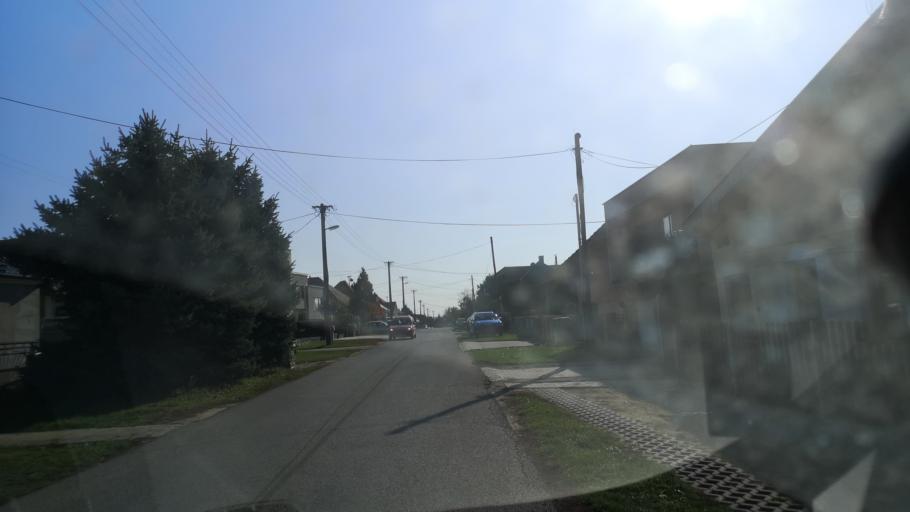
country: SK
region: Nitriansky
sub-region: Okres Nitra
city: Nitra
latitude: 48.3109
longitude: 17.9442
